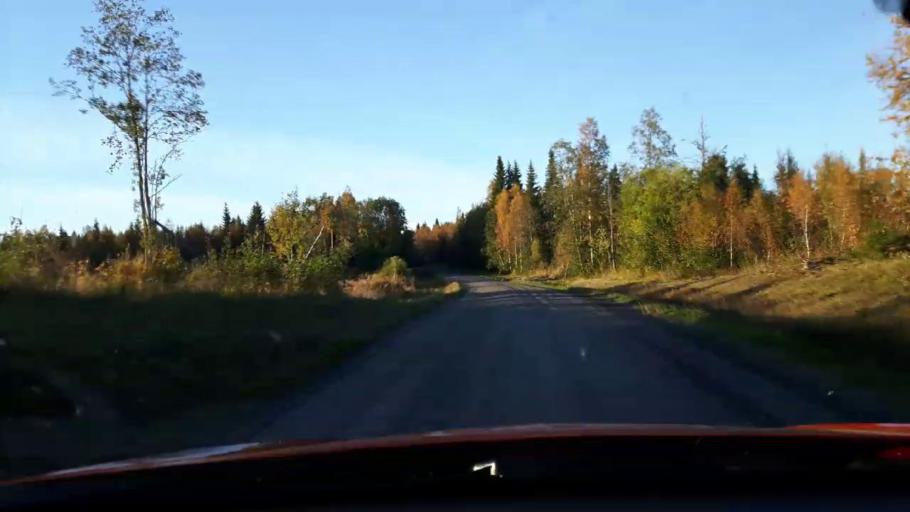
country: SE
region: Jaemtland
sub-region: Krokoms Kommun
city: Krokom
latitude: 63.4294
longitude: 14.6110
